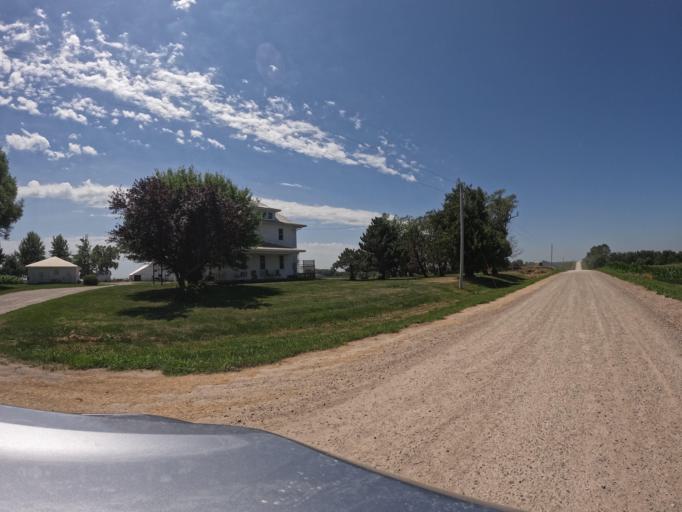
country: US
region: Iowa
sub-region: Poweshiek County
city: Montezuma
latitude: 41.4666
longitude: -92.3659
